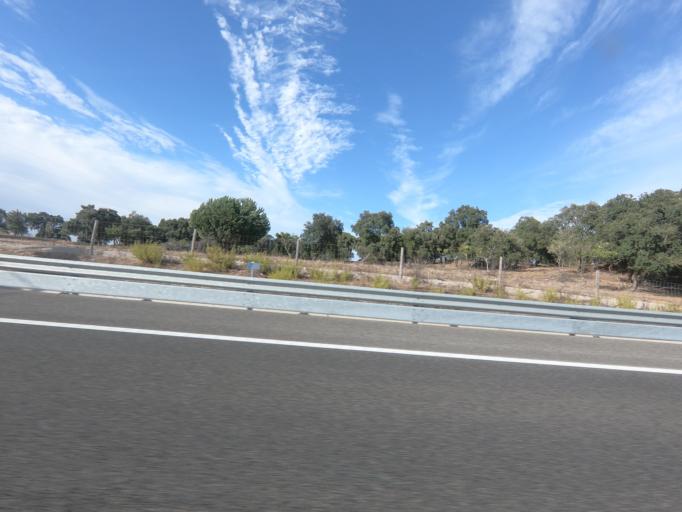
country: PT
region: Setubal
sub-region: Barreiro
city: Santo Antonio da Charneca
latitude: 38.5987
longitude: -9.0399
